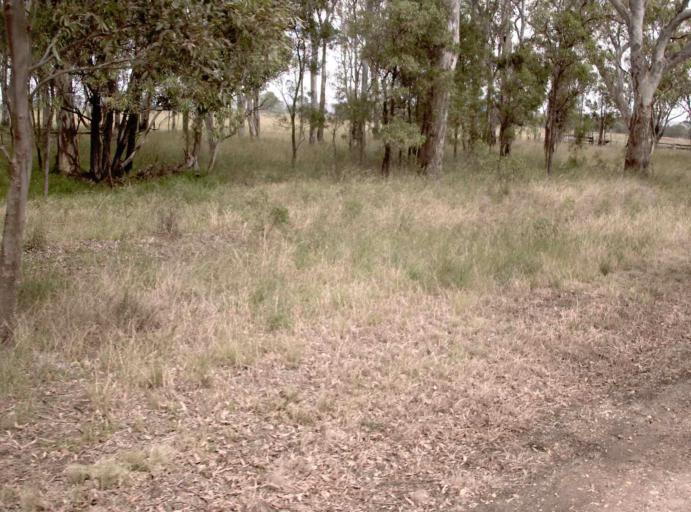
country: AU
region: Victoria
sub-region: Wellington
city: Sale
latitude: -37.9077
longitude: 147.0785
